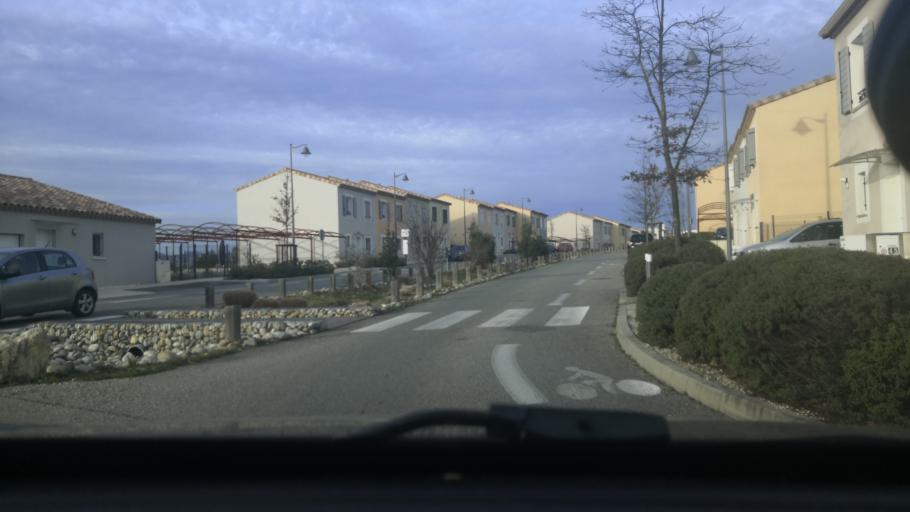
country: FR
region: Rhone-Alpes
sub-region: Departement de la Drome
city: Montelimar
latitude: 44.5371
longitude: 4.7685
